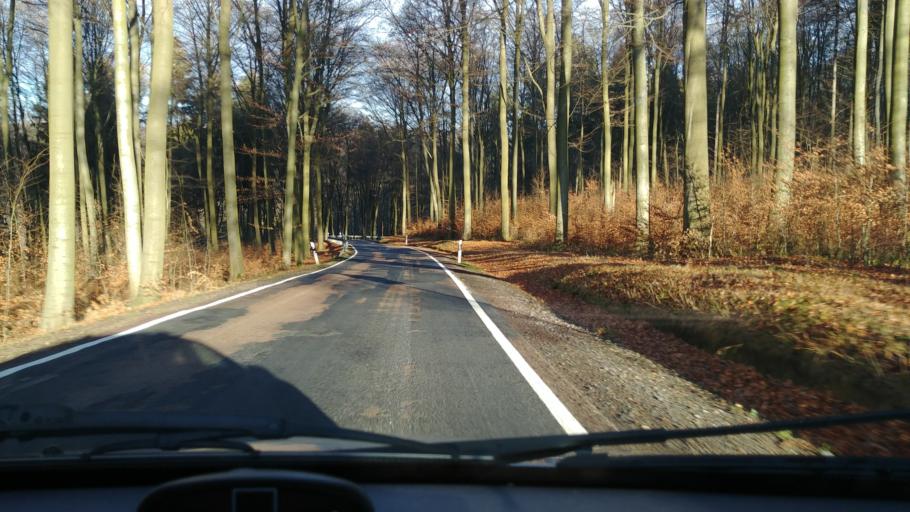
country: DE
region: Rheinland-Pfalz
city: Attenhausen
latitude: 50.2760
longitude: 7.8641
